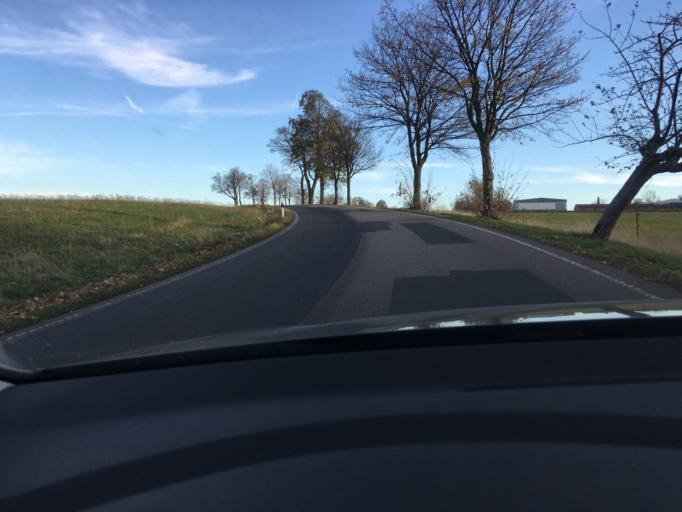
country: DE
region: Saxony
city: Barenstein
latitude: 50.8223
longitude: 13.8077
